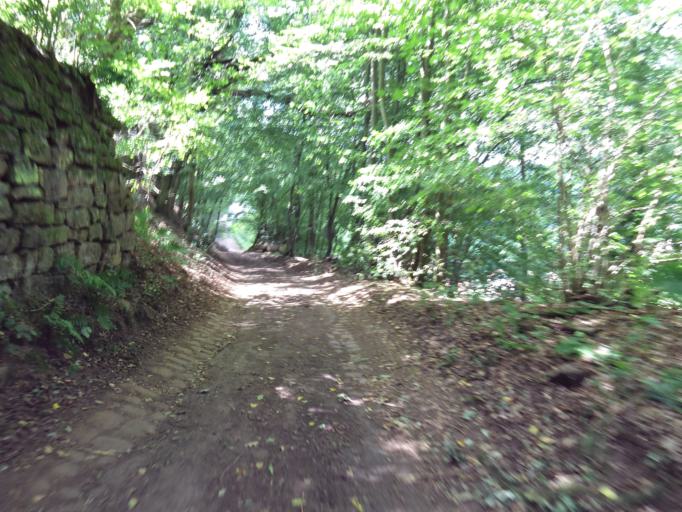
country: DE
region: Rheinland-Pfalz
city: Frankenstein
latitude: 49.4256
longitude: 7.9910
